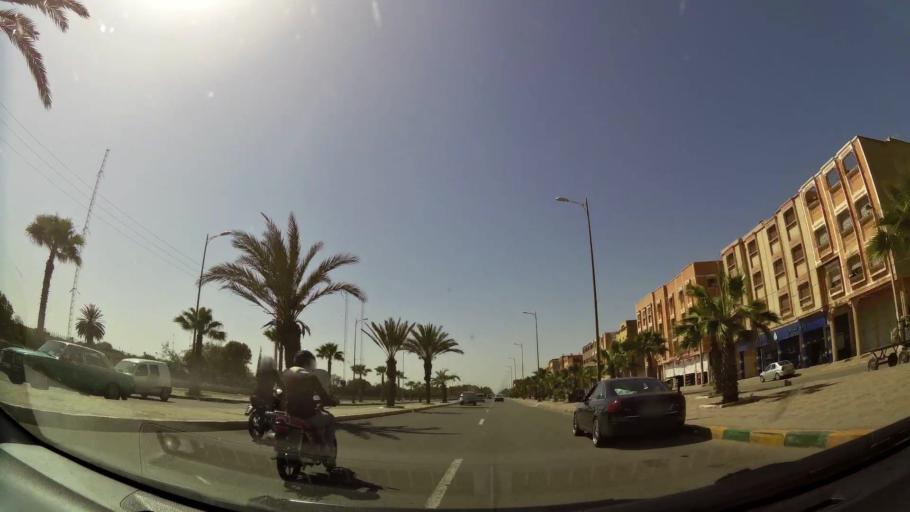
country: MA
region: Souss-Massa-Draa
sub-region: Inezgane-Ait Mellou
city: Inezgane
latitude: 30.3303
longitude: -9.5039
